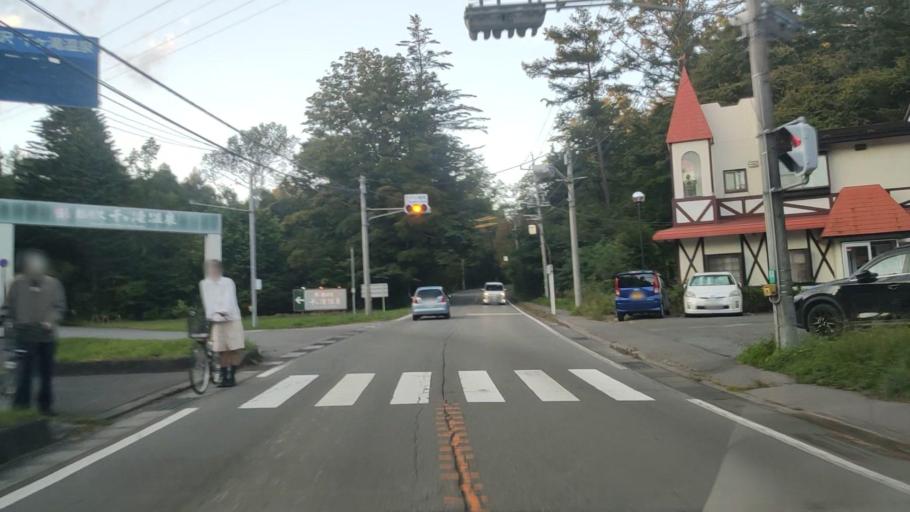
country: JP
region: Nagano
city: Komoro
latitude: 36.3623
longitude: 138.5878
